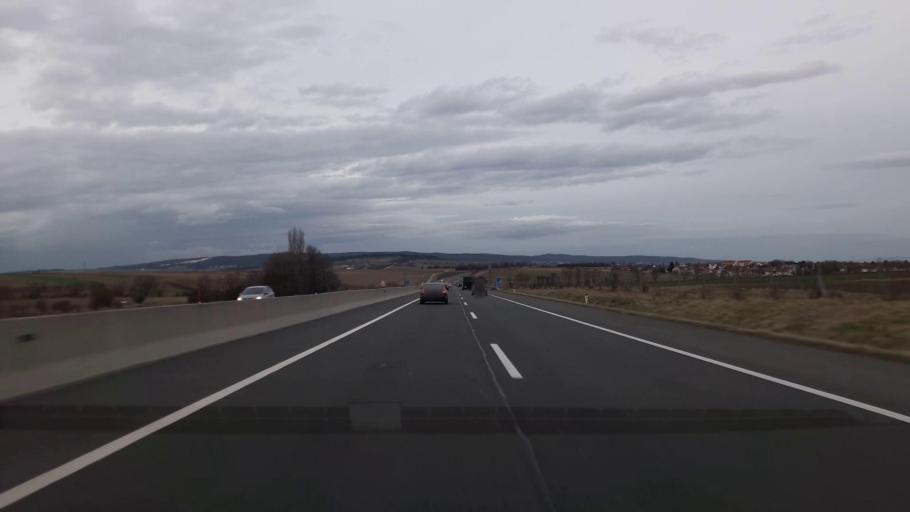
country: AT
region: Burgenland
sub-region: Politischer Bezirk Mattersburg
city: Hirm
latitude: 47.7825
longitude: 16.4379
